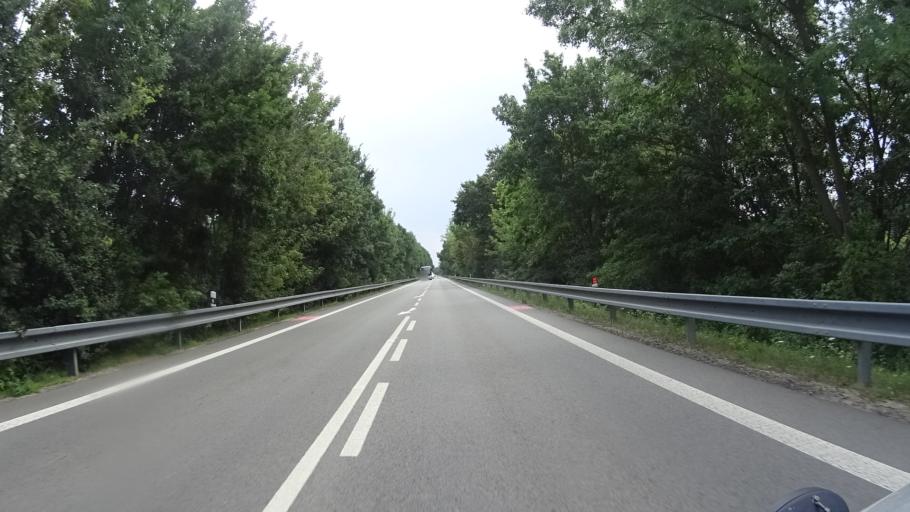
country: CZ
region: South Moravian
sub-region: Okres Breclav
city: Lednice
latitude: 48.8181
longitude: 16.8162
